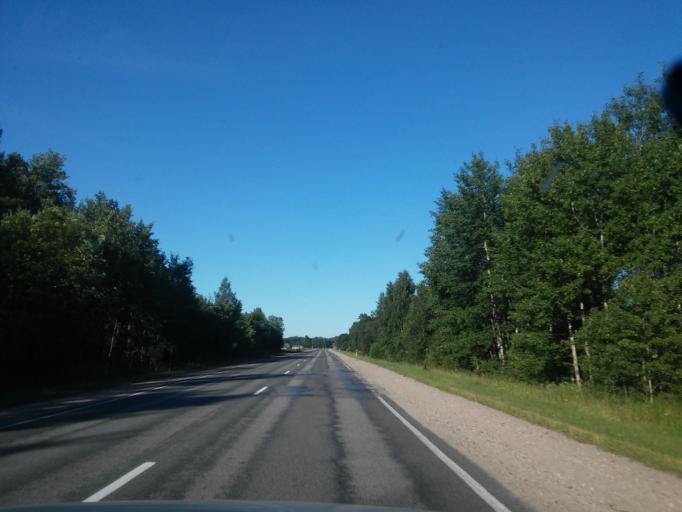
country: LV
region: Skrunda
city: Skrunda
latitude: 56.6756
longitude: 22.0420
